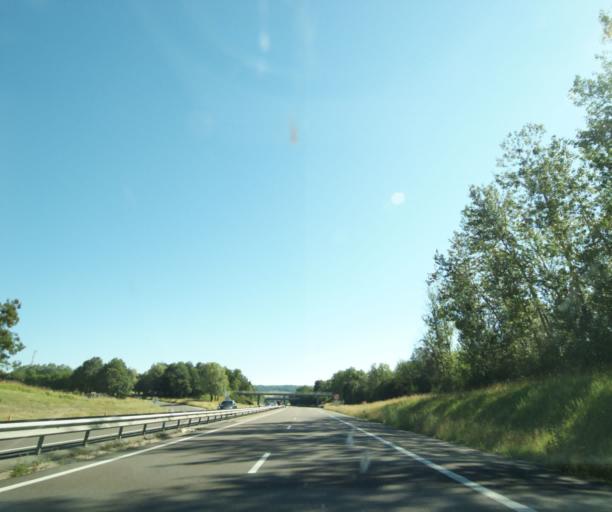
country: FR
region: Champagne-Ardenne
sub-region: Departement de la Haute-Marne
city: Rolampont
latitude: 47.9293
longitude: 5.2862
